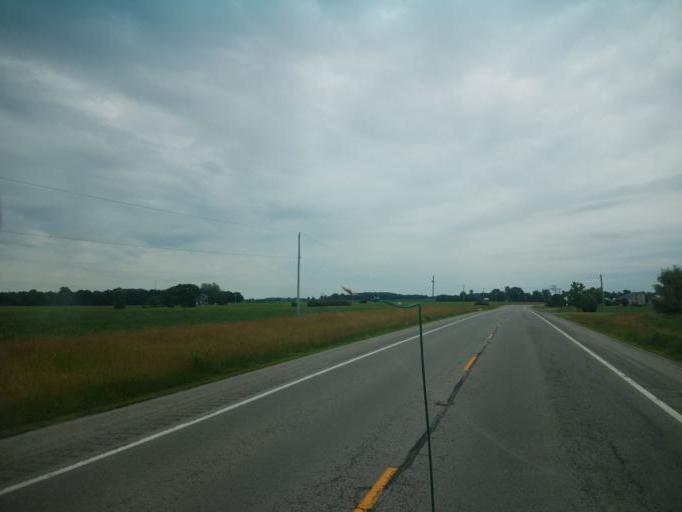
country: US
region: Ohio
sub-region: Hardin County
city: Ada
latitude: 40.7244
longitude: -83.7801
